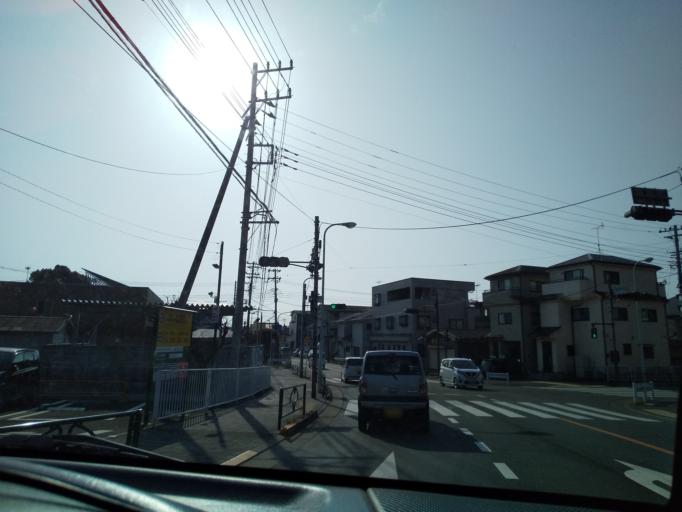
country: JP
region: Tokyo
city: Fussa
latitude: 35.7282
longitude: 139.3145
